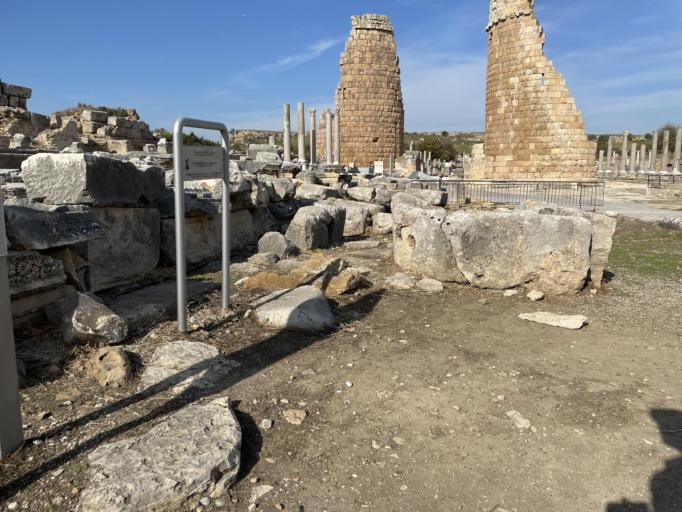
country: TR
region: Antalya
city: Aksu
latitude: 36.9608
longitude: 30.8540
